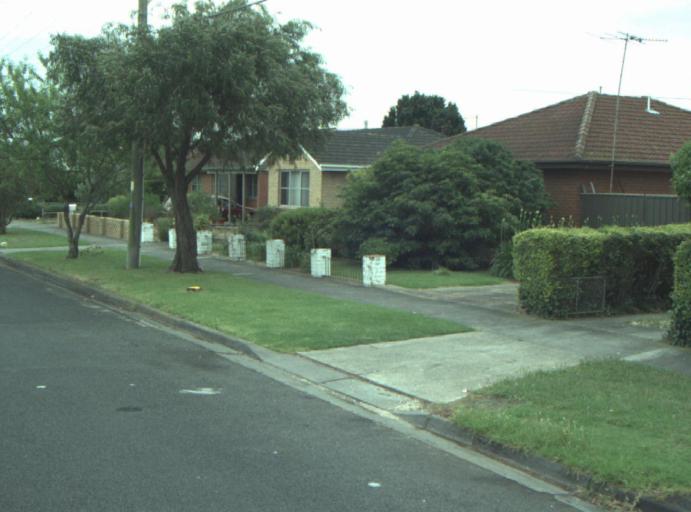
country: AU
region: Victoria
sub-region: Greater Geelong
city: East Geelong
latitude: -38.1658
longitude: 144.3983
